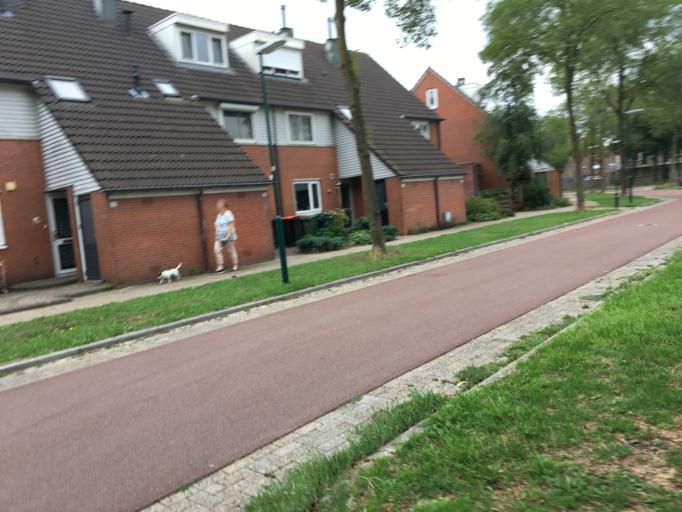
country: NL
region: Utrecht
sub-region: Gemeente Houten
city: Houten
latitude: 52.0410
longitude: 5.1767
